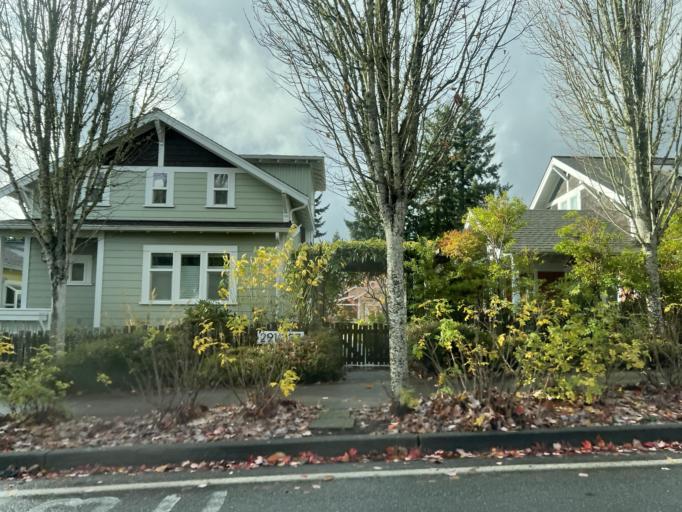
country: US
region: Washington
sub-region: Kitsap County
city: Bainbridge Island
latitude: 47.6268
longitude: -122.5170
